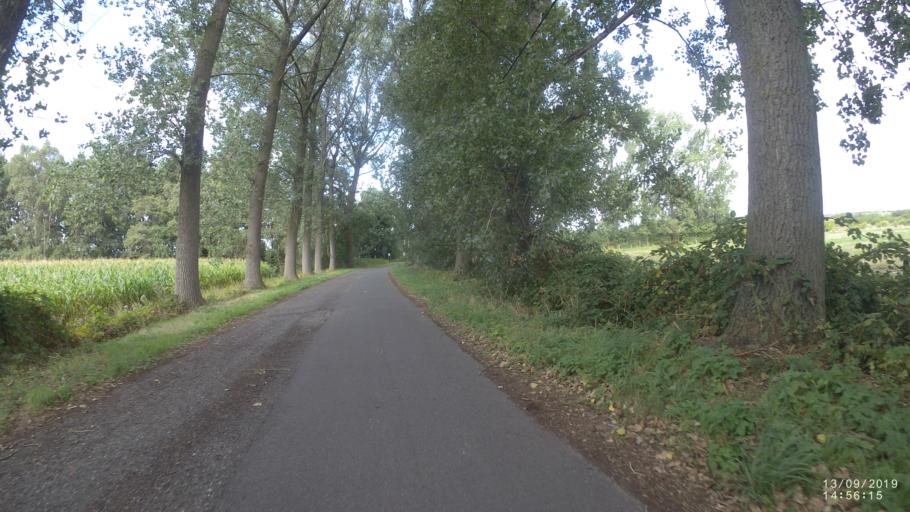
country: BE
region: Flanders
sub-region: Provincie Oost-Vlaanderen
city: Zelzate
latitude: 51.1938
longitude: 3.7766
